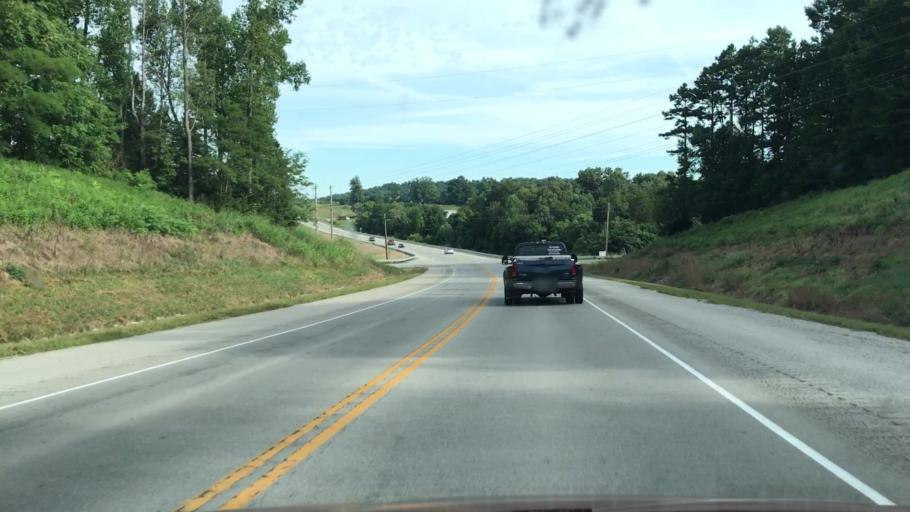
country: US
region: Kentucky
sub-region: Edmonson County
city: Brownsville
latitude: 37.1594
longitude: -86.2221
